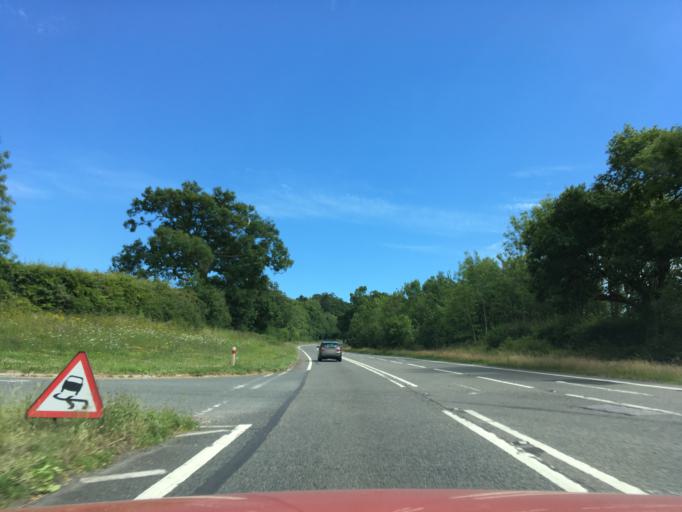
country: GB
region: England
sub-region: Somerset
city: Yeovil
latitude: 50.8598
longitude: -2.5922
